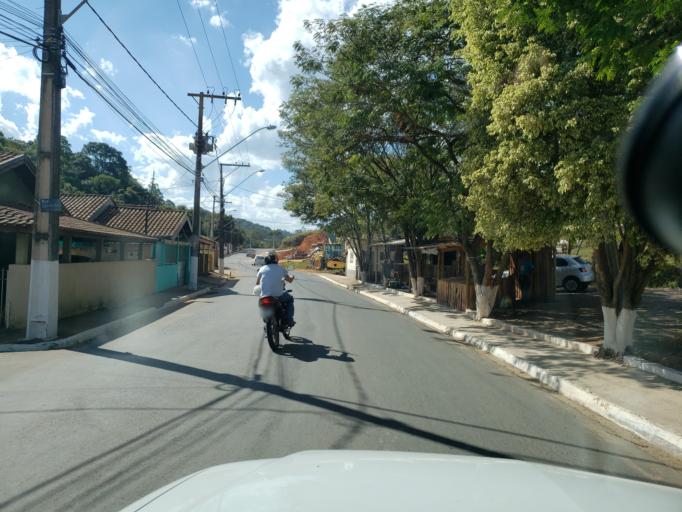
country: BR
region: Minas Gerais
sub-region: Monte Siao
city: Monte Siao
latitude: -22.4238
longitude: -46.5679
